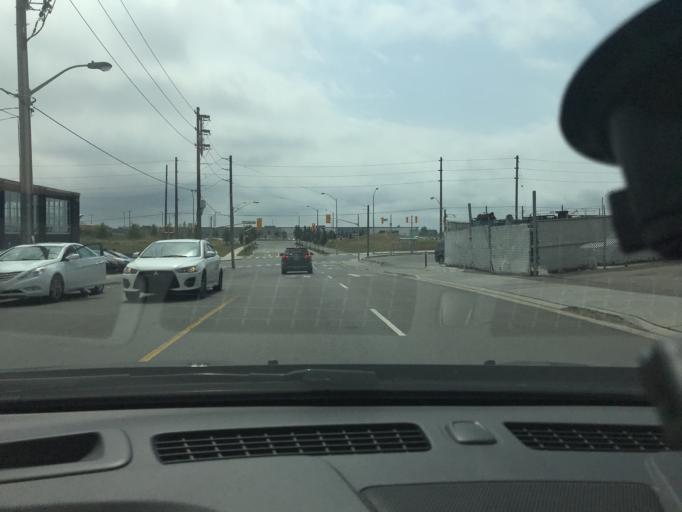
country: CA
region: Ontario
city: Concord
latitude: 43.7551
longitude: -79.4804
